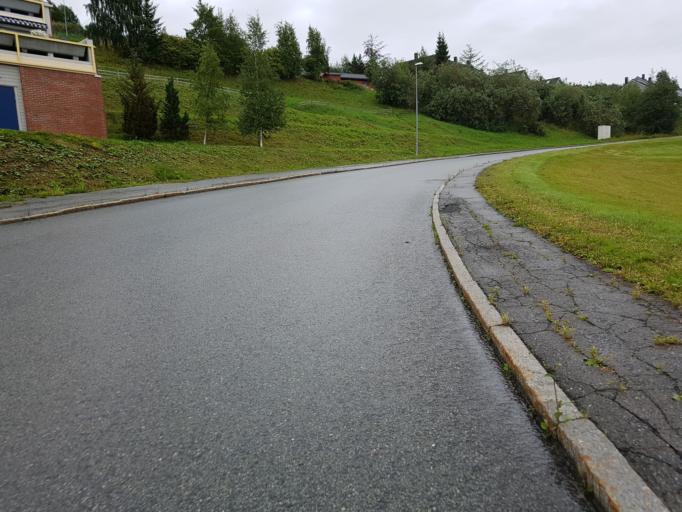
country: NO
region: Sor-Trondelag
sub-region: Trondheim
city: Trondheim
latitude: 63.3991
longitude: 10.4400
